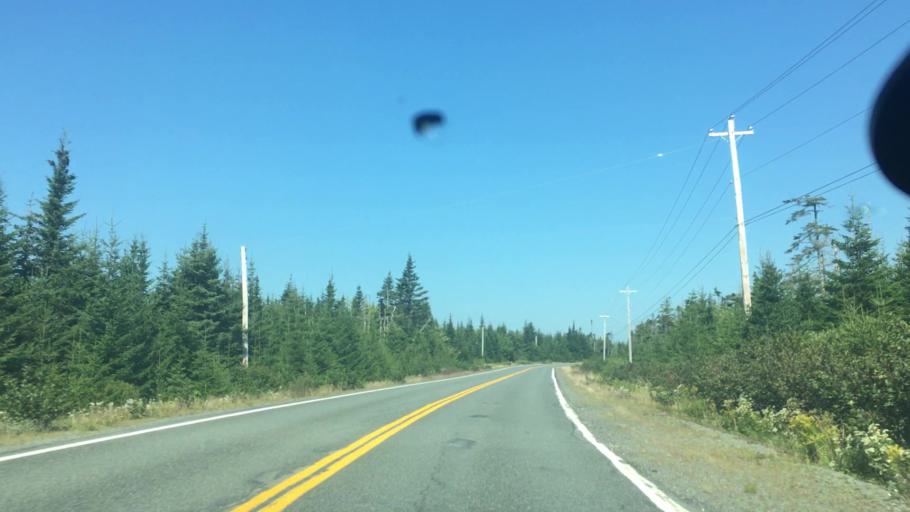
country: CA
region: Nova Scotia
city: Antigonish
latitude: 44.9849
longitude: -62.0965
